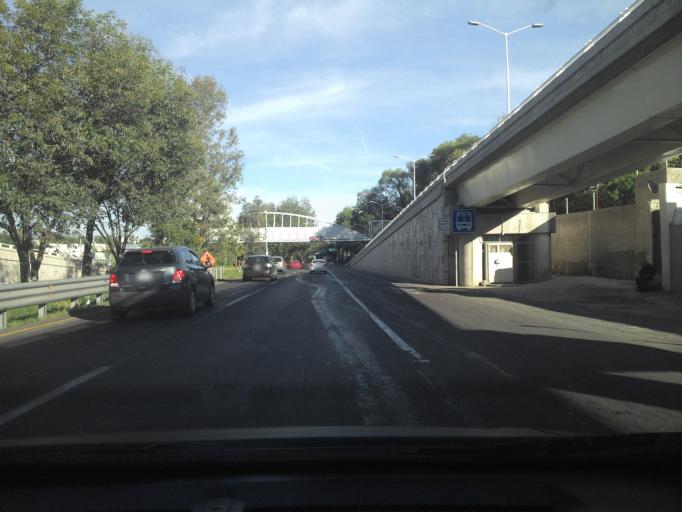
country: MX
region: Jalisco
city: Nuevo Mexico
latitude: 20.7179
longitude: -103.4821
